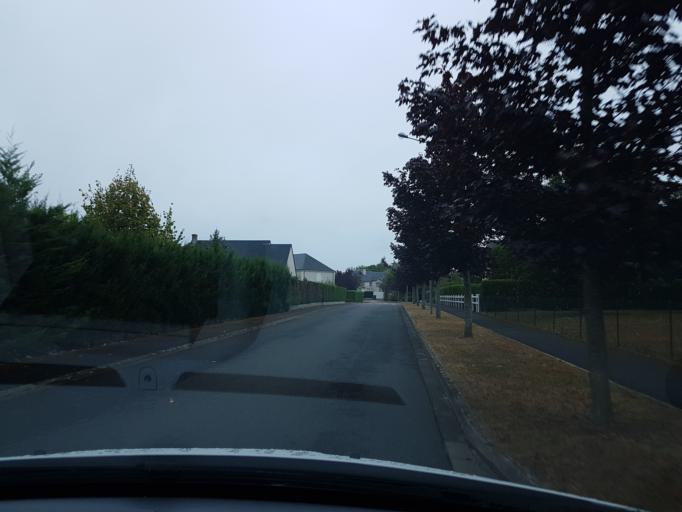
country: FR
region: Centre
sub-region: Departement d'Indre-et-Loire
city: Saint-Avertin
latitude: 47.3614
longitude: 0.7444
